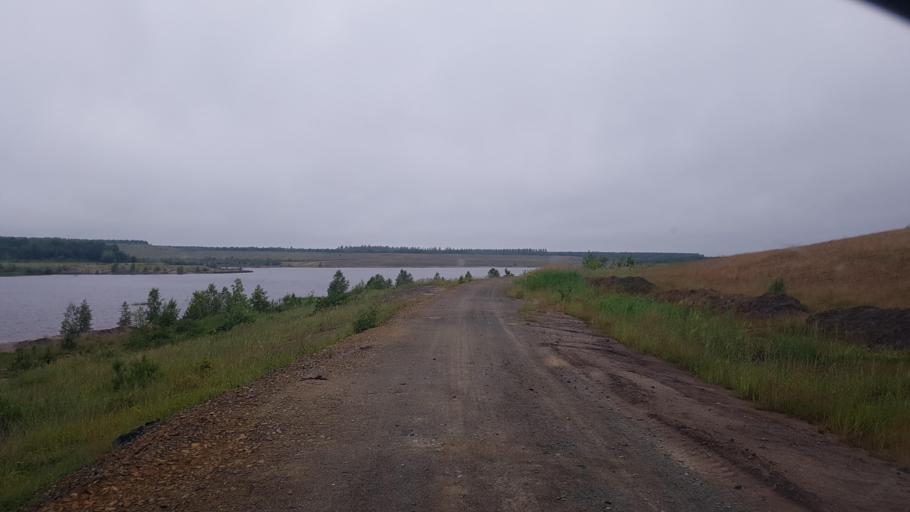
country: DE
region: Brandenburg
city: Lauchhammer
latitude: 51.5398
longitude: 13.7393
